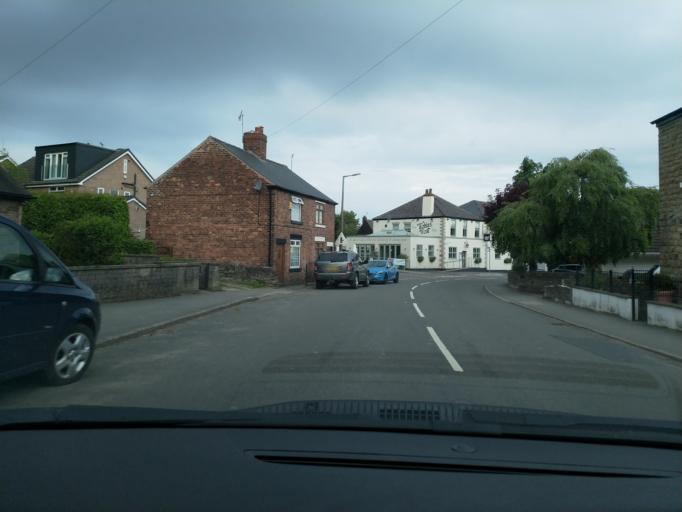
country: GB
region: England
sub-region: Derbyshire
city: Dronfield
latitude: 53.2743
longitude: -1.4948
